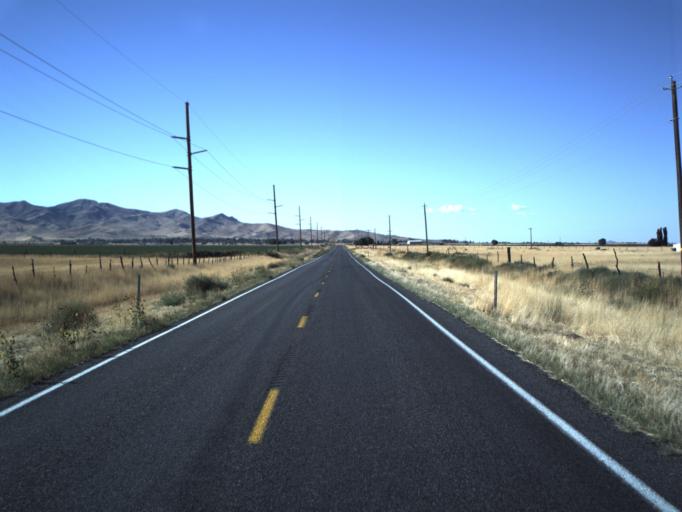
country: US
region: Utah
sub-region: Millard County
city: Delta
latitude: 39.4175
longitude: -112.3293
